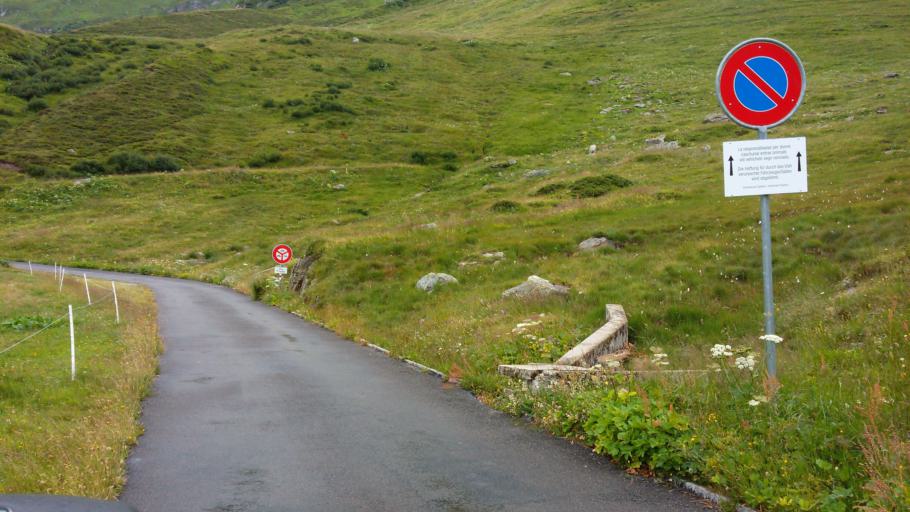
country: CH
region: Uri
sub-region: Uri
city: Andermatt
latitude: 46.6496
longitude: 8.6816
